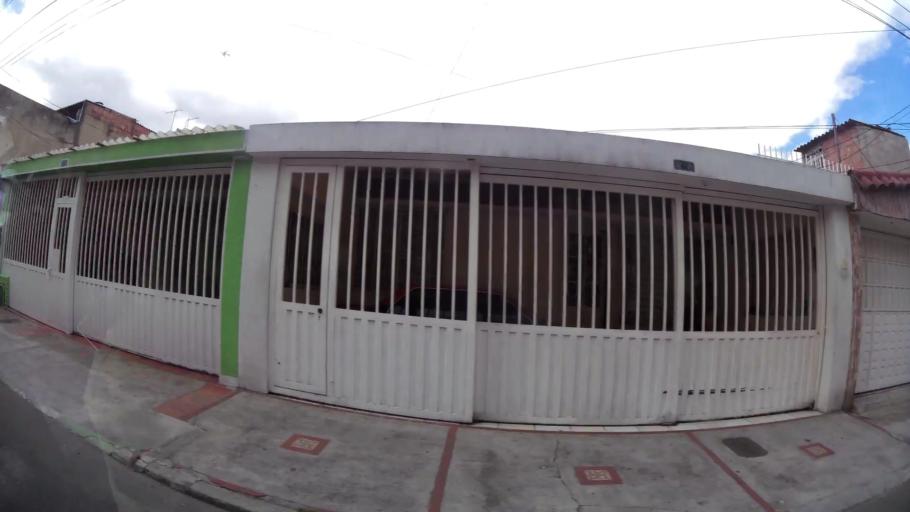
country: CO
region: Bogota D.C.
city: Bogota
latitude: 4.6056
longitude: -74.1301
